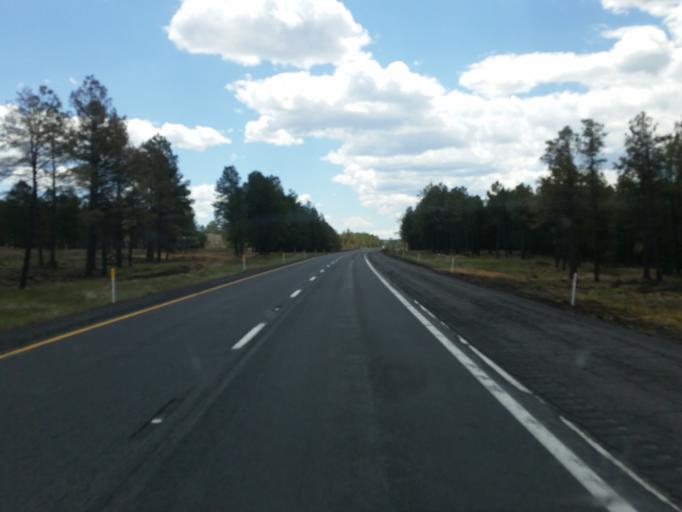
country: US
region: Arizona
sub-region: Coconino County
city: Flagstaff
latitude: 35.2218
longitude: -111.7938
